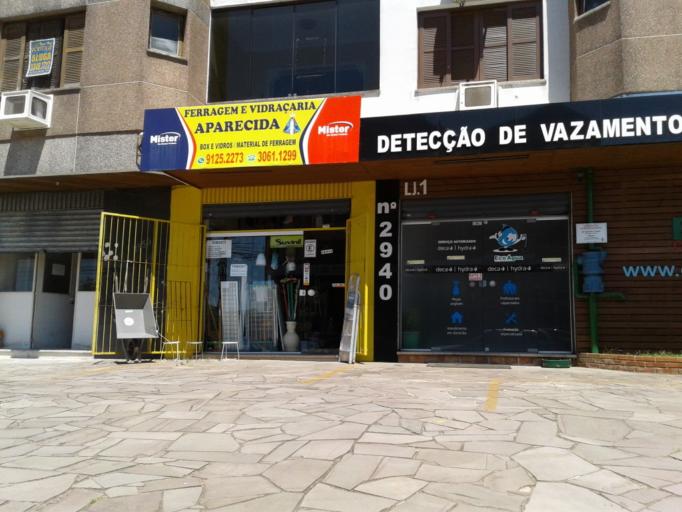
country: BR
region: Rio Grande do Sul
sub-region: Cachoeirinha
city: Cachoeirinha
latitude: -30.0160
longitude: -51.1312
